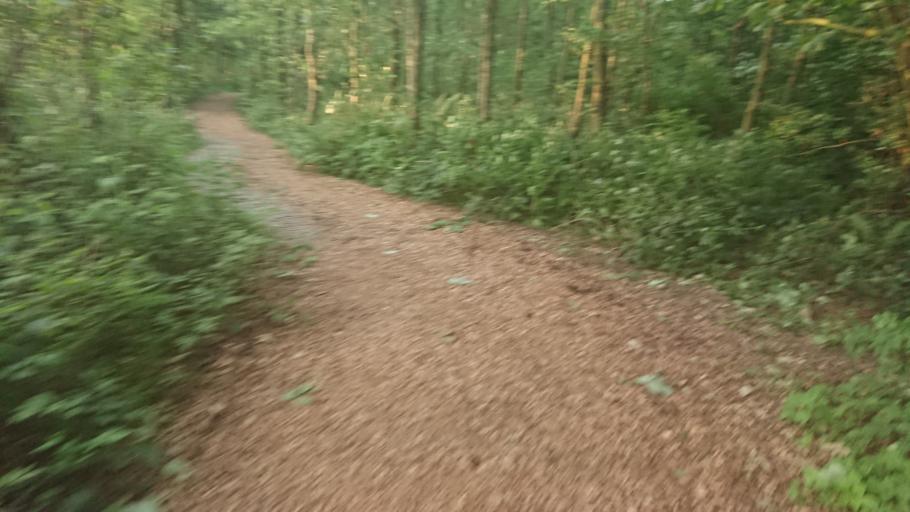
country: GB
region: England
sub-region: Lancashire
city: Galgate
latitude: 54.0003
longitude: -2.7863
